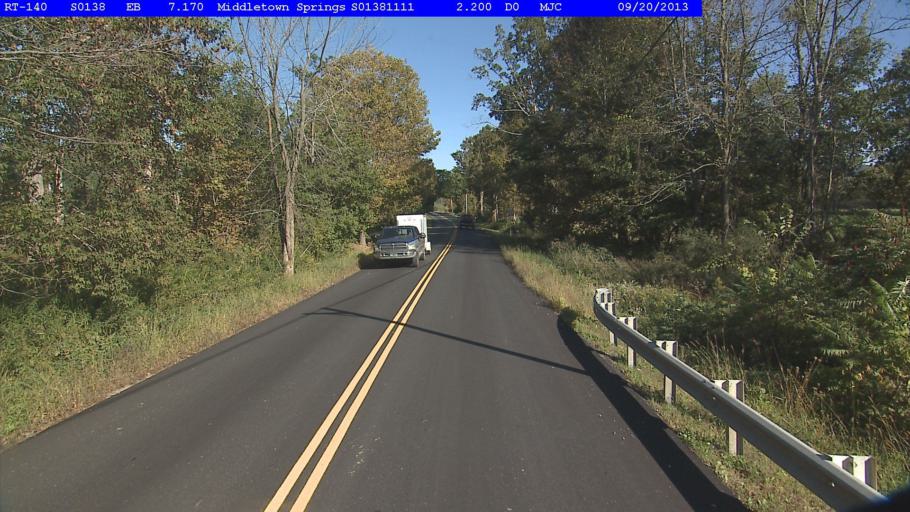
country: US
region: Vermont
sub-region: Rutland County
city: Poultney
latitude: 43.4840
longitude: -73.1378
